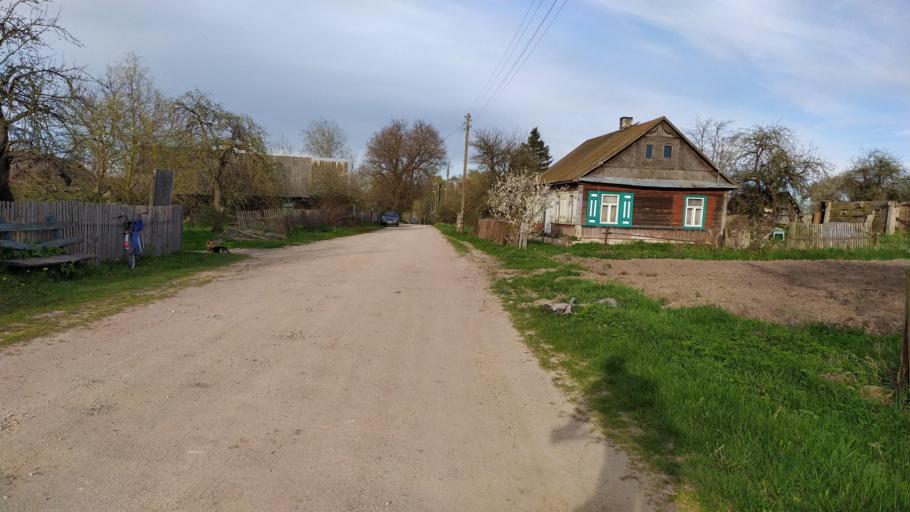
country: BY
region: Brest
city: Kamyanyets
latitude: 52.4093
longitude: 23.6700
